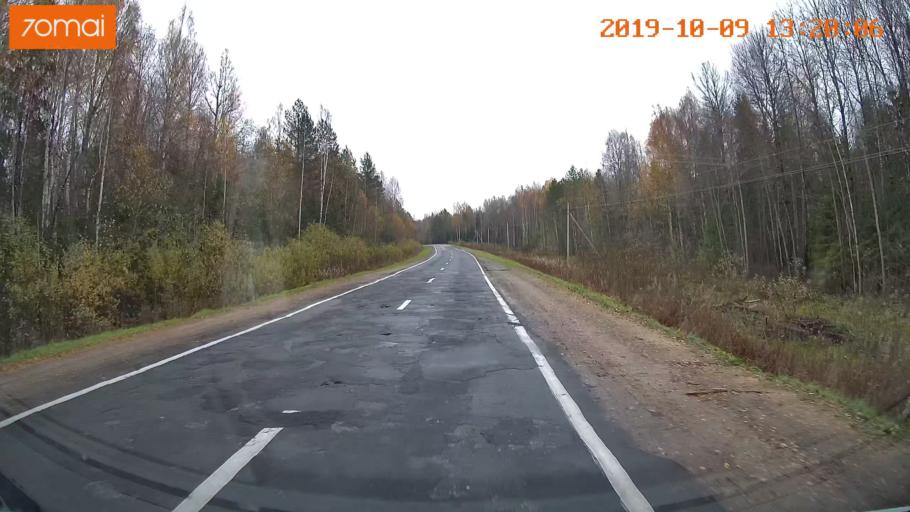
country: RU
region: Jaroslavl
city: Lyubim
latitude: 58.3450
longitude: 40.8252
